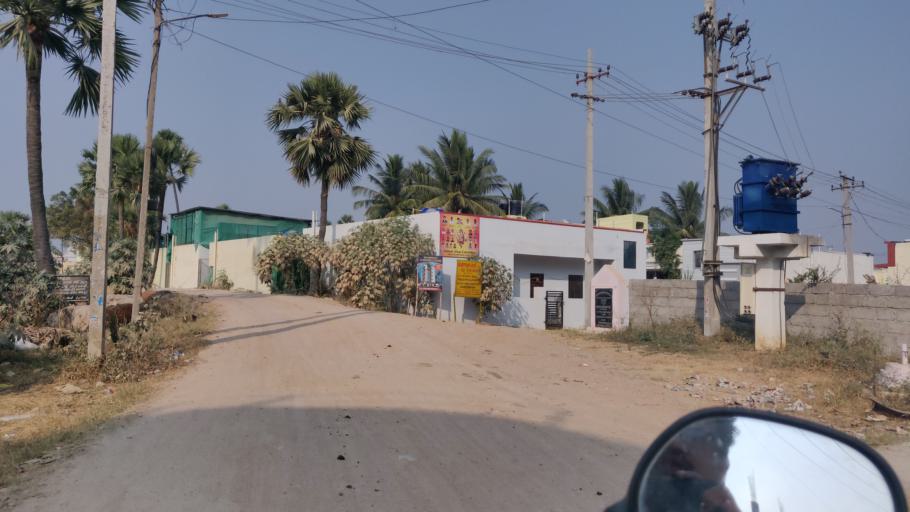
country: IN
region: Telangana
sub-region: Rangareddi
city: Uppal Kalan
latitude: 17.3919
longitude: 78.6037
